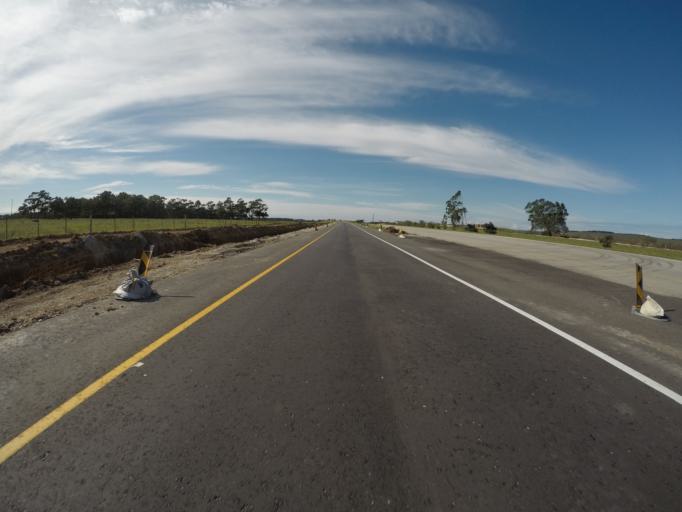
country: ZA
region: Eastern Cape
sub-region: Nelson Mandela Bay Metropolitan Municipality
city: Uitenhage
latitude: -33.9179
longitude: 25.2893
